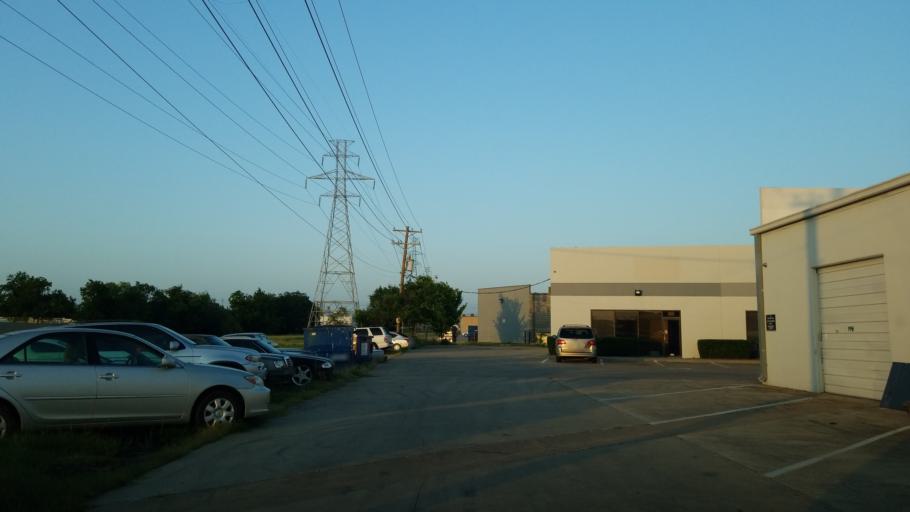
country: US
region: Texas
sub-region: Dallas County
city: Farmers Branch
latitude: 32.8836
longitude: -96.8894
